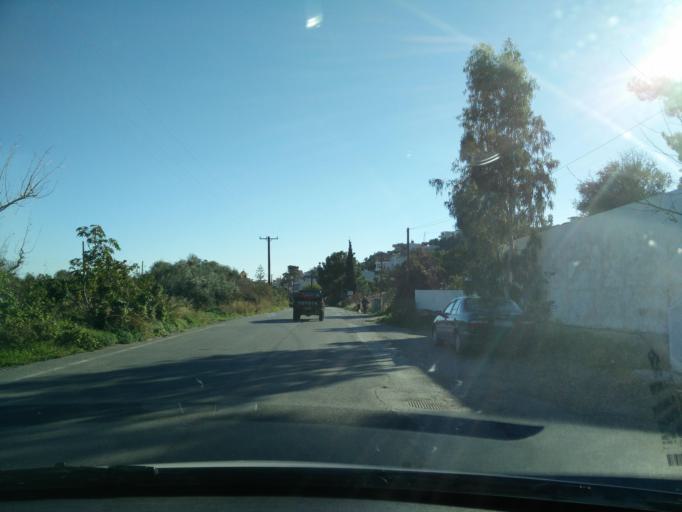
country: GR
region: Crete
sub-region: Nomos Lasithiou
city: Gra Liyia
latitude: 35.0081
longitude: 25.5836
